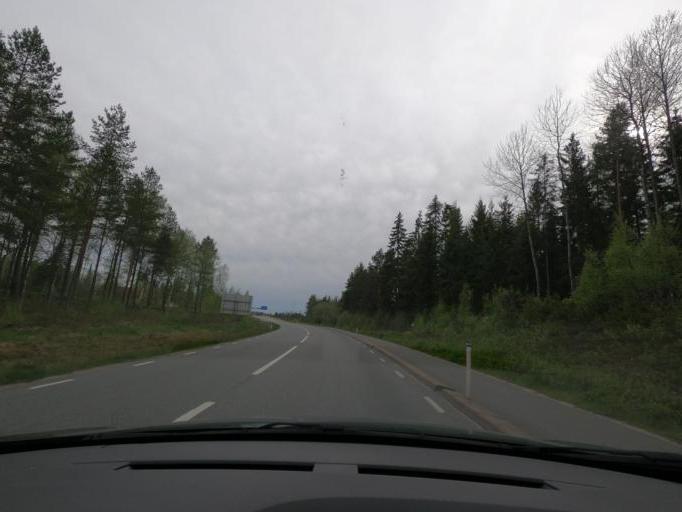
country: SE
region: Joenkoeping
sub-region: Varnamo Kommun
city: Bredaryd
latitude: 57.1840
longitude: 13.7512
